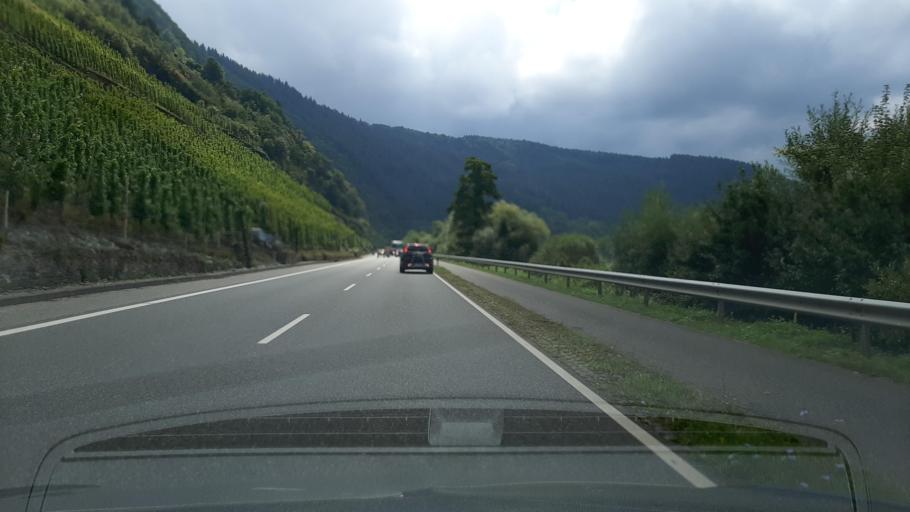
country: DE
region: Rheinland-Pfalz
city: Starkenburg
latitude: 49.9606
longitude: 7.1345
